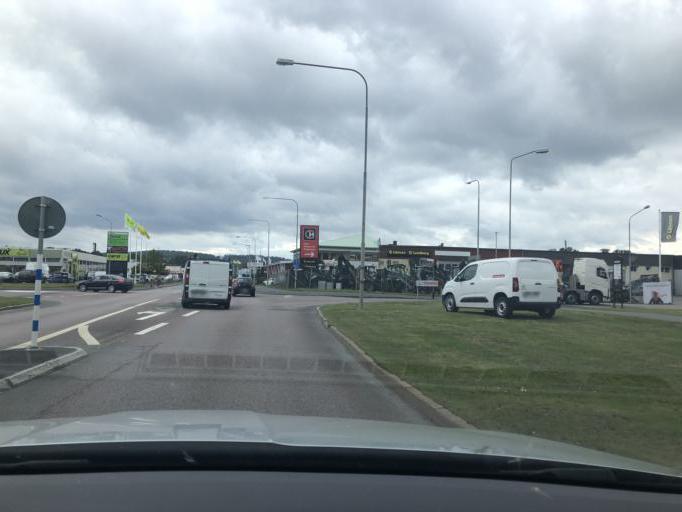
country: SE
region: Joenkoeping
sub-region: Jonkopings Kommun
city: Jonkoping
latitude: 57.7658
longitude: 14.1790
